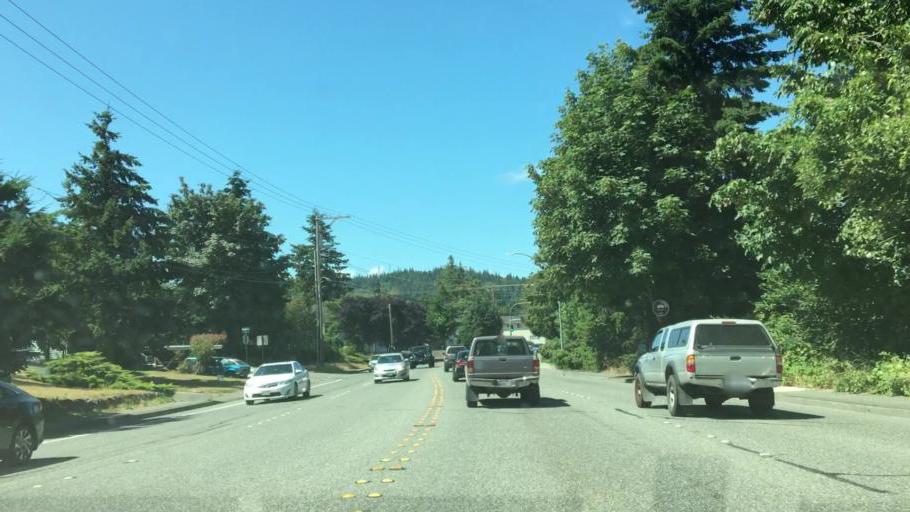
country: US
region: Washington
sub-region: Whatcom County
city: Bellingham
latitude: 48.7446
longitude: -122.4538
